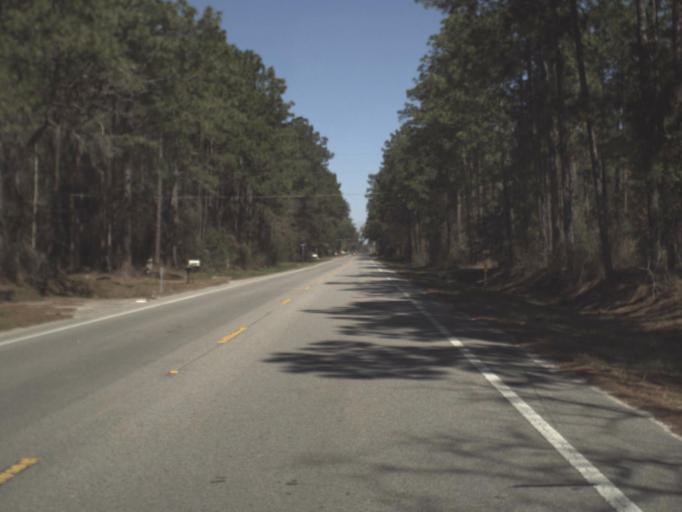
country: US
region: Florida
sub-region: Leon County
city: Woodville
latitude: 30.3163
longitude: -84.3116
